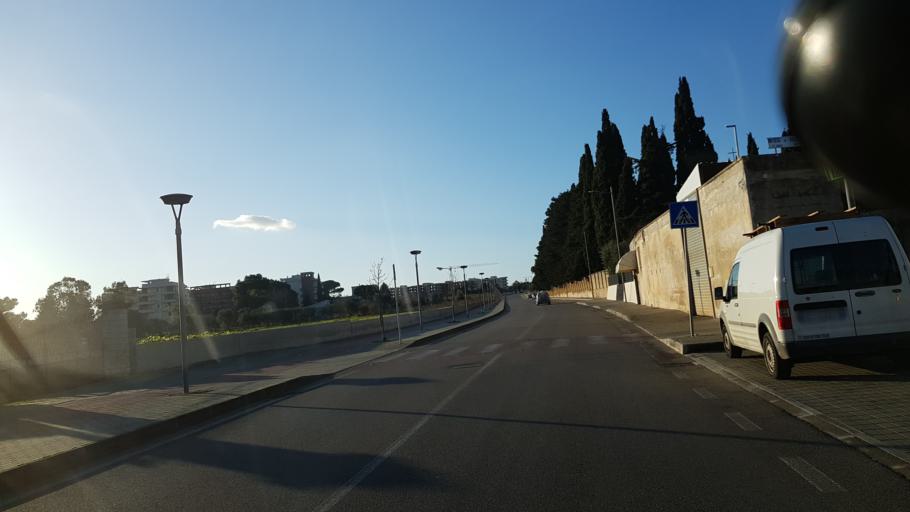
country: IT
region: Apulia
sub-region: Provincia di Bari
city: Gioia del Colle
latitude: 40.8009
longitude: 16.9139
